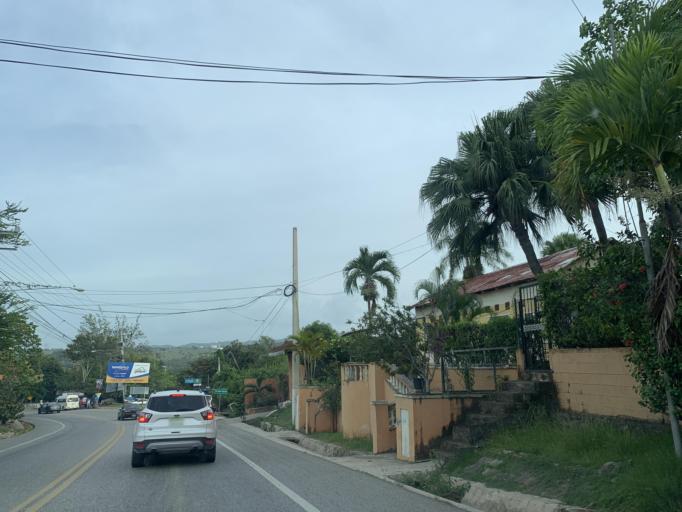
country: DO
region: Puerto Plata
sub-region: Puerto Plata
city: Puerto Plata
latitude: 19.7210
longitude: -70.6205
